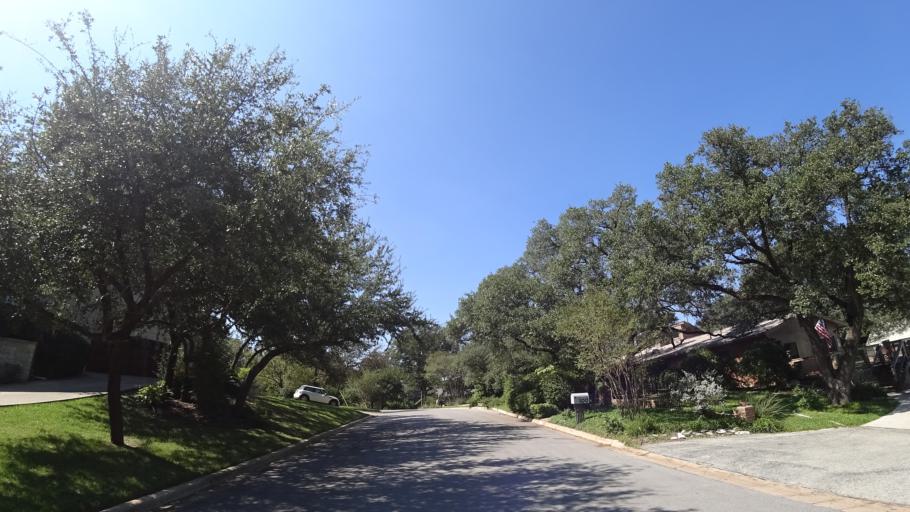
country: US
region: Texas
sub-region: Travis County
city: Rollingwood
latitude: 30.2781
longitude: -97.7825
